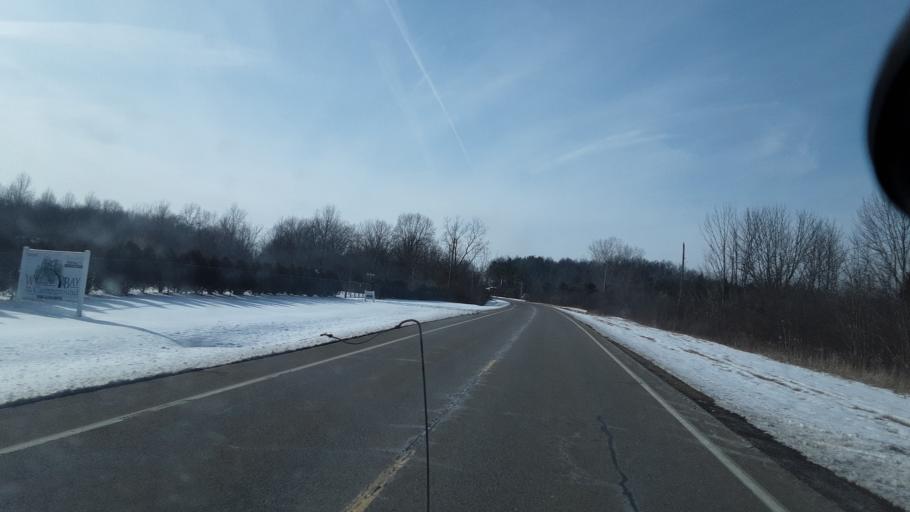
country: US
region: Ohio
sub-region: Mahoning County
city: Craig Beach
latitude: 41.0233
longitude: -81.0080
